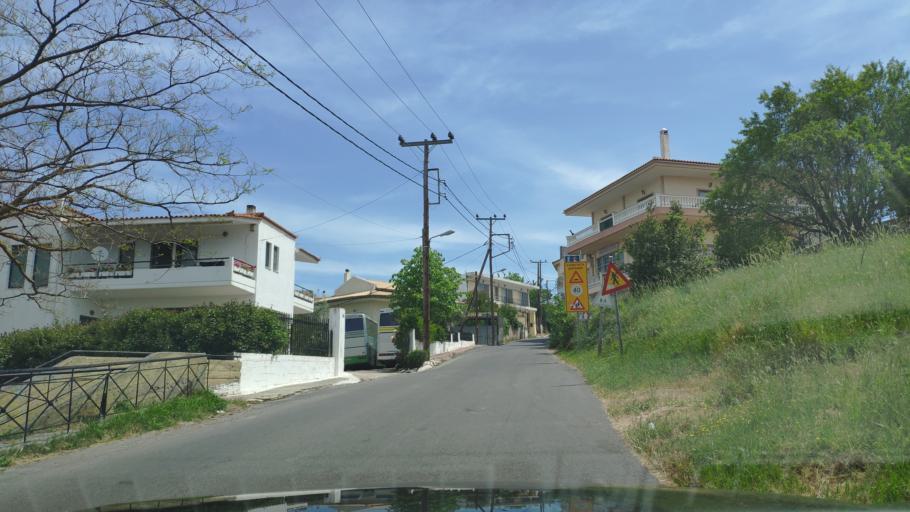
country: GR
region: Attica
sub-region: Nomarchia Anatolikis Attikis
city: Varnavas
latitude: 38.2224
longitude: 23.9213
